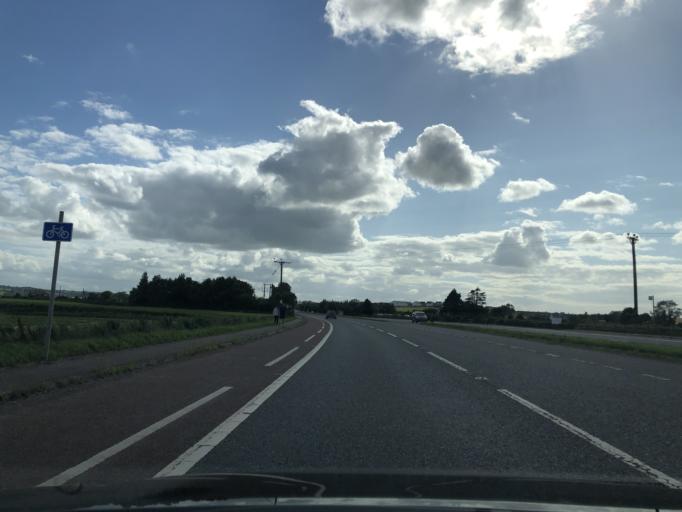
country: GB
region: Northern Ireland
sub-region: Ards District
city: Comber
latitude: 54.5583
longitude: -5.7151
